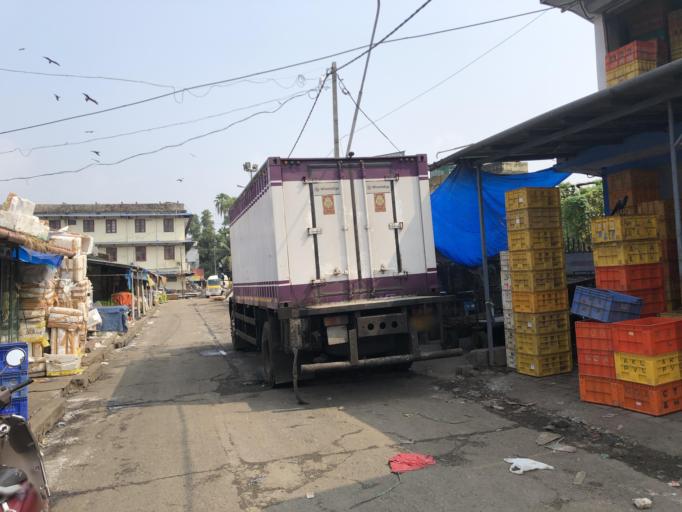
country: IN
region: Kerala
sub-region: Kozhikode
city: Kozhikode
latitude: 11.2507
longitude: 75.7781
